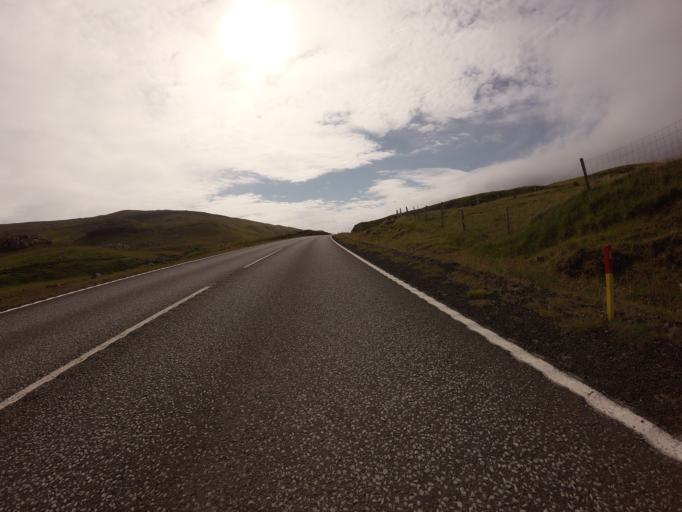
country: FO
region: Sandoy
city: Sandur
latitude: 61.8942
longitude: -6.8657
